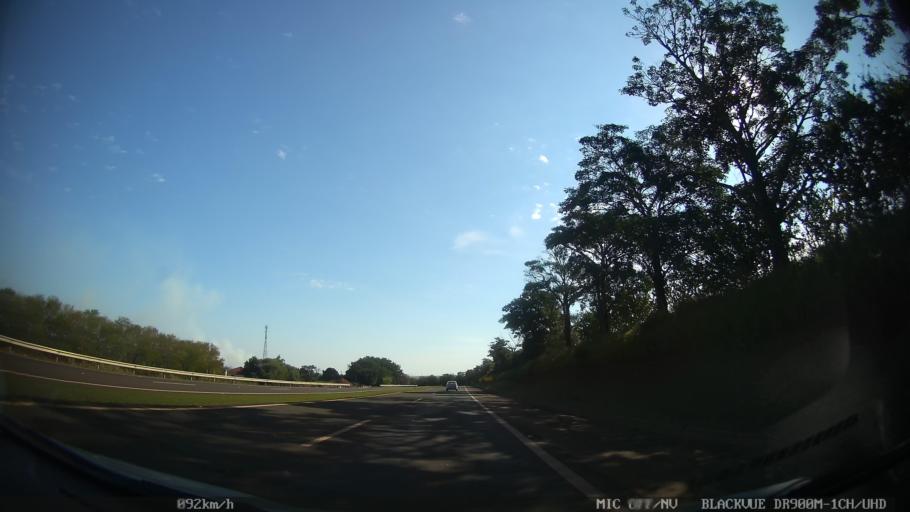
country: BR
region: Sao Paulo
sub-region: Iracemapolis
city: Iracemapolis
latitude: -22.6692
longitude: -47.5489
